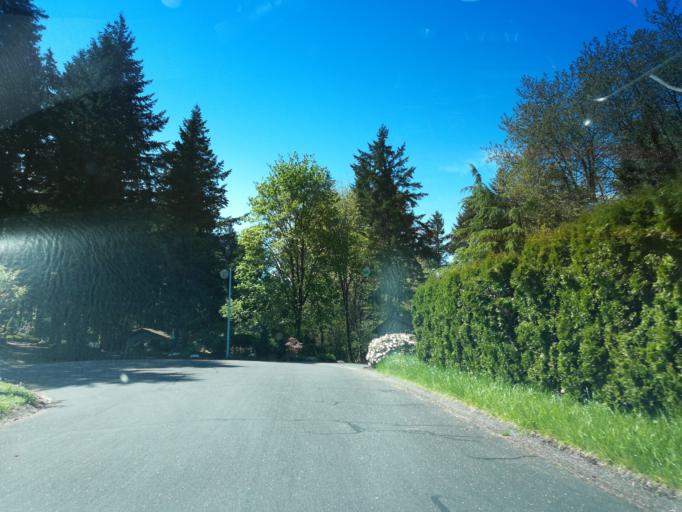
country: US
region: Oregon
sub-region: Clackamas County
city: Damascus
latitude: 45.4311
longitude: -122.4311
